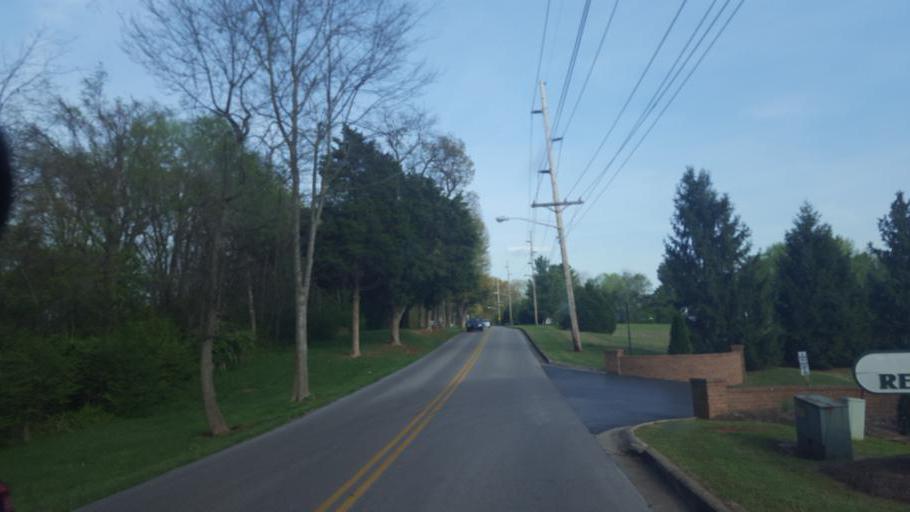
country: US
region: Kentucky
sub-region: Warren County
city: Bowling Green
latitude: 36.9507
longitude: -86.4139
